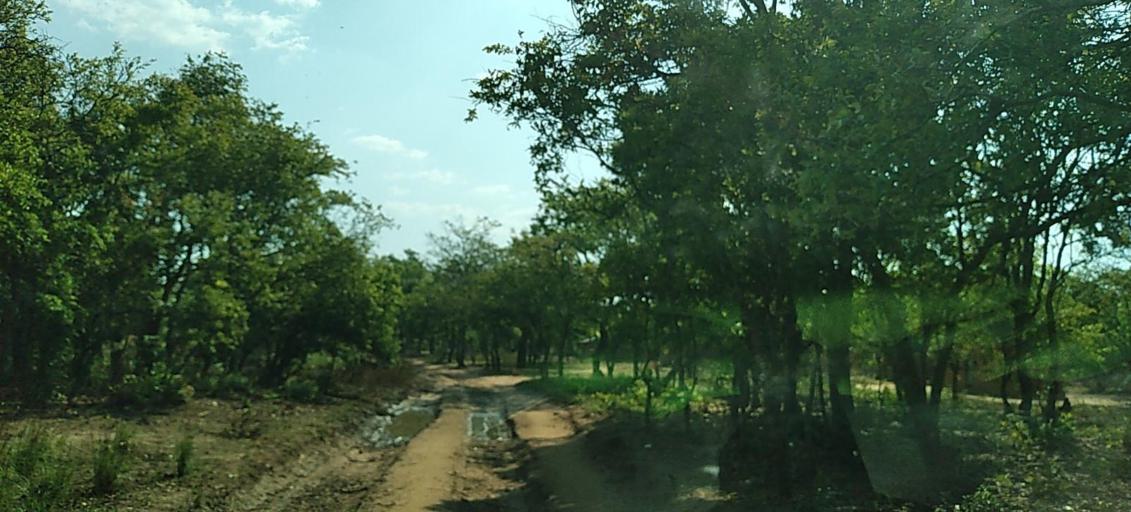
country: ZM
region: North-Western
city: Mwinilunga
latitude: -11.2982
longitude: 24.8545
